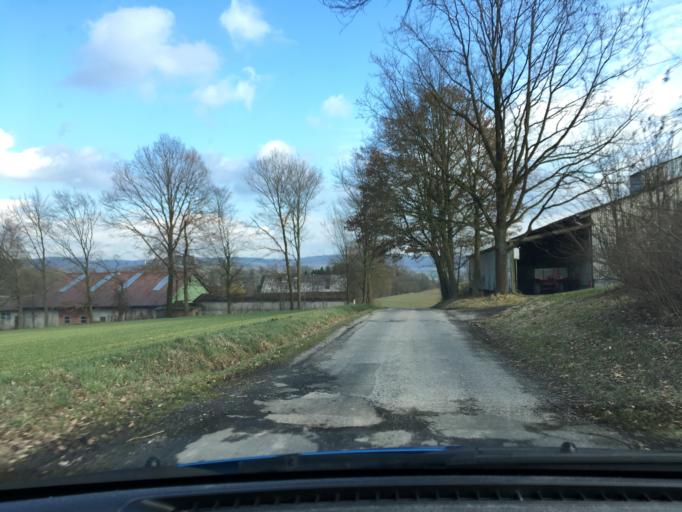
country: DE
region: Lower Saxony
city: Uslar
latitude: 51.6439
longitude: 9.6317
